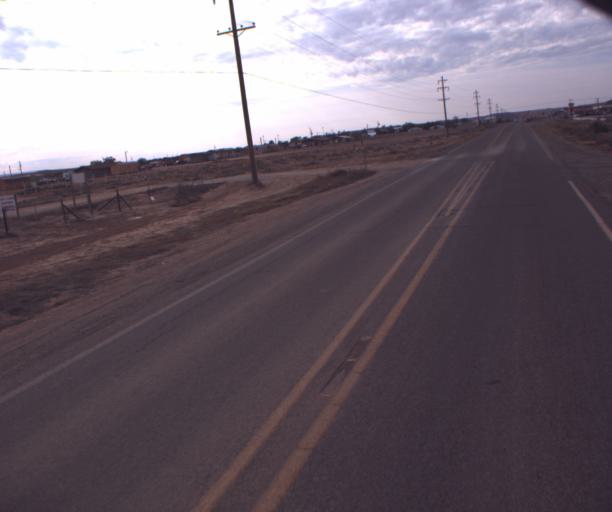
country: US
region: Arizona
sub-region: Apache County
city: Many Farms
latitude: 36.3565
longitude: -109.6165
